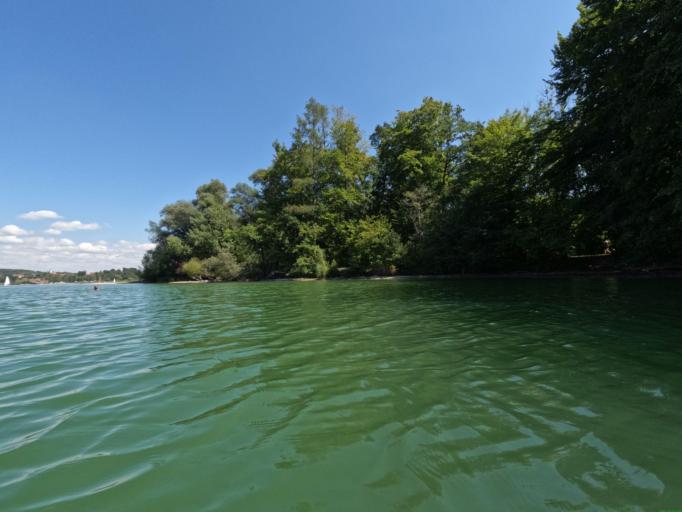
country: DE
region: Bavaria
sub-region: Upper Bavaria
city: Waging am See
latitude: 47.9470
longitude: 12.7410
